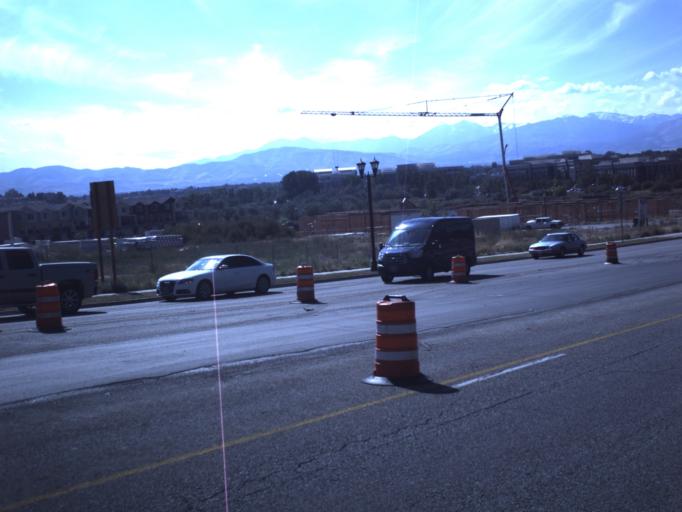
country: US
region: Utah
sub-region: Salt Lake County
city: South Jordan
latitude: 40.5590
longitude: -111.9038
